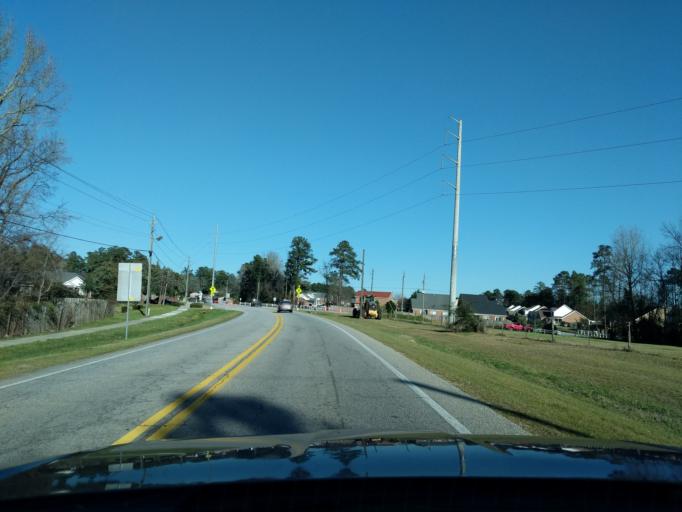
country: US
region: Georgia
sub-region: Columbia County
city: Grovetown
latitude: 33.4515
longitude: -82.2147
